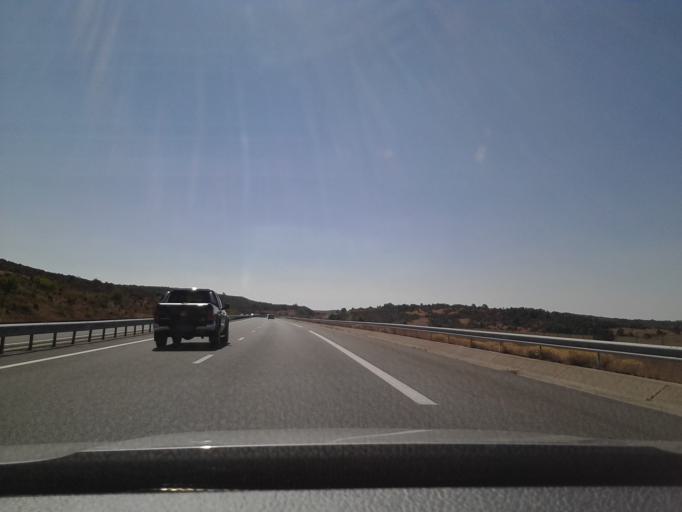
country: FR
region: Midi-Pyrenees
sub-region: Departement de l'Aveyron
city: Creissels
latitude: 44.0579
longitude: 3.0337
